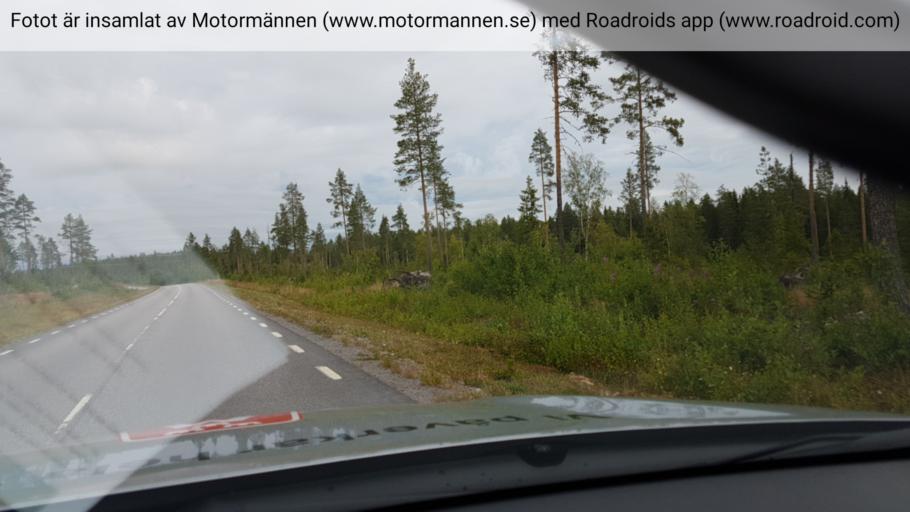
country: SE
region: Norrbotten
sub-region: Bodens Kommun
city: Saevast
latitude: 65.6741
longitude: 21.6540
